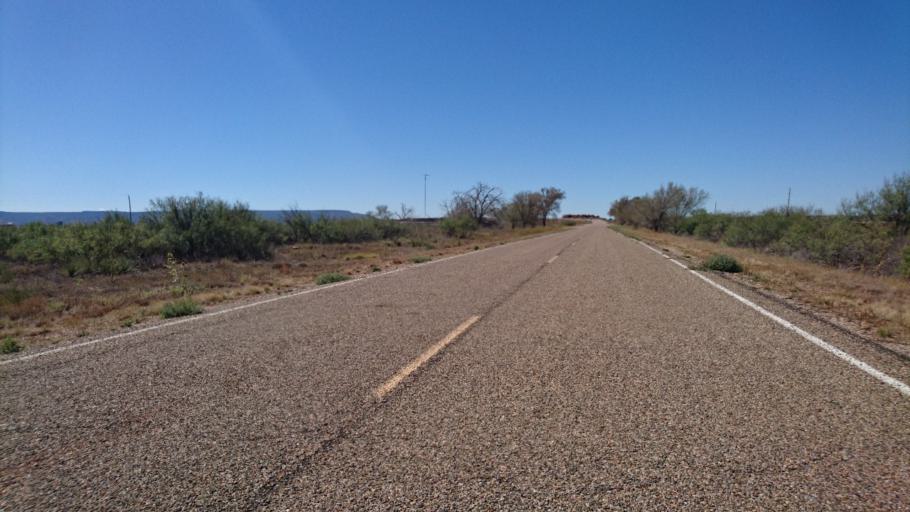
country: US
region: New Mexico
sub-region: Quay County
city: Tucumcari
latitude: 35.0964
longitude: -104.0633
